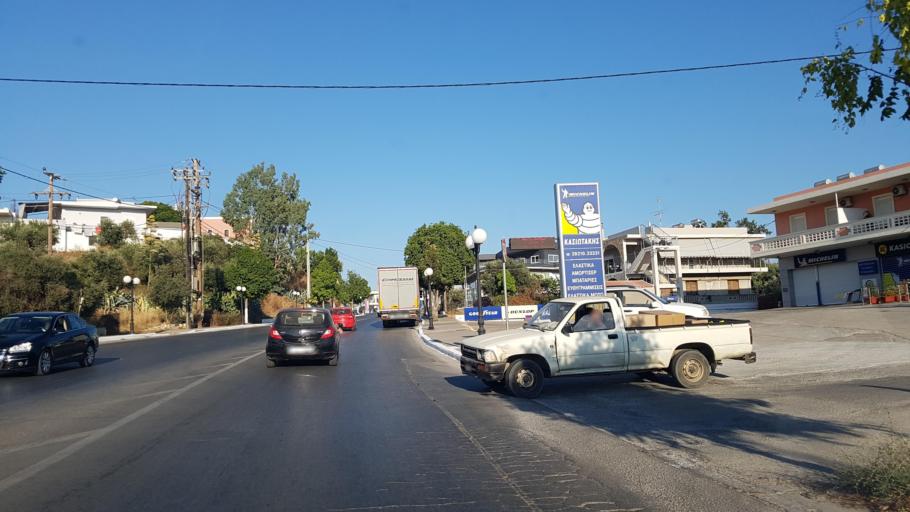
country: GR
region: Crete
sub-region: Nomos Chanias
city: Daratsos
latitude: 35.5072
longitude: 23.9822
